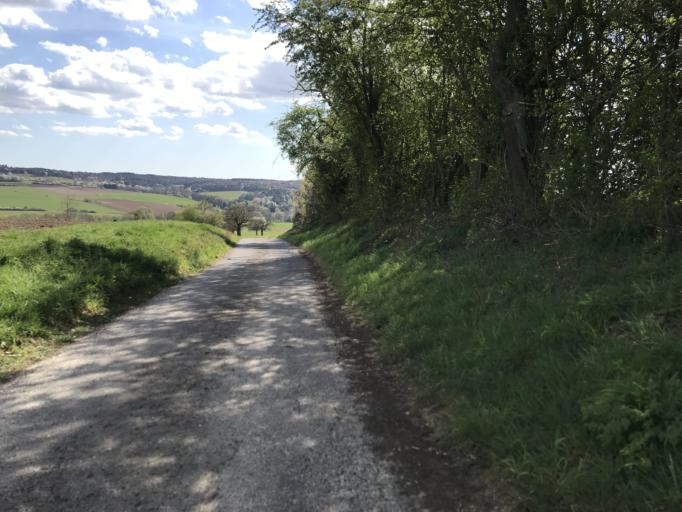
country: DE
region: Hesse
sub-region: Regierungsbezirk Giessen
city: Rabenau
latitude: 50.6869
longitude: 8.8368
